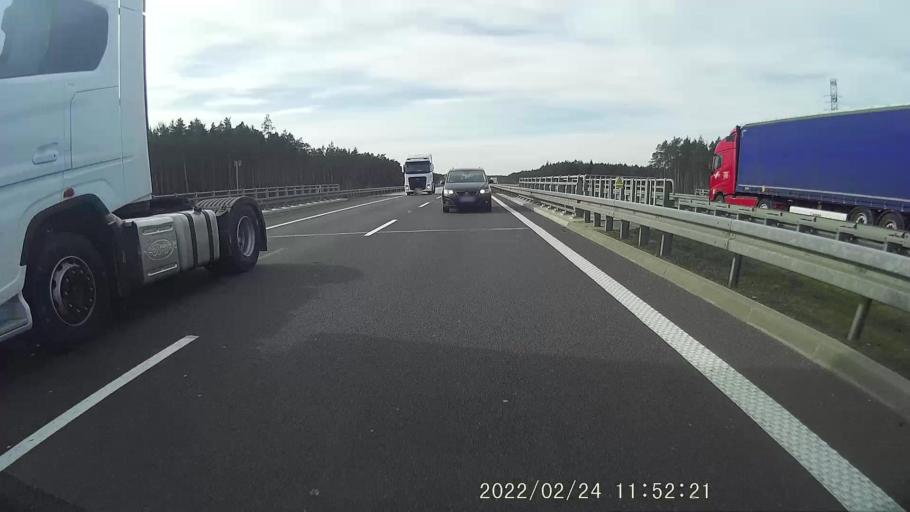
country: PL
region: Lower Silesian Voivodeship
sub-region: Powiat polkowicki
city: Radwanice
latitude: 51.6205
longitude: 15.9762
